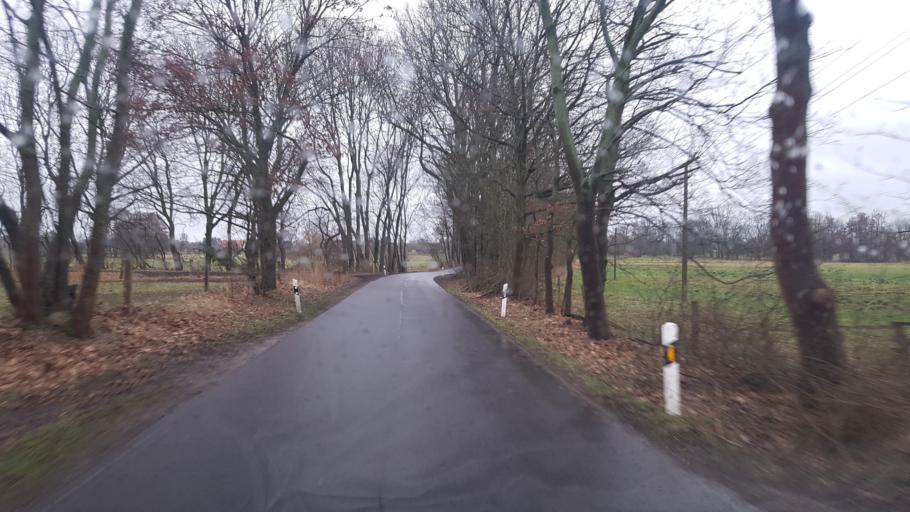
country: DE
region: Brandenburg
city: Oranienburg
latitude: 52.8789
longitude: 13.2169
